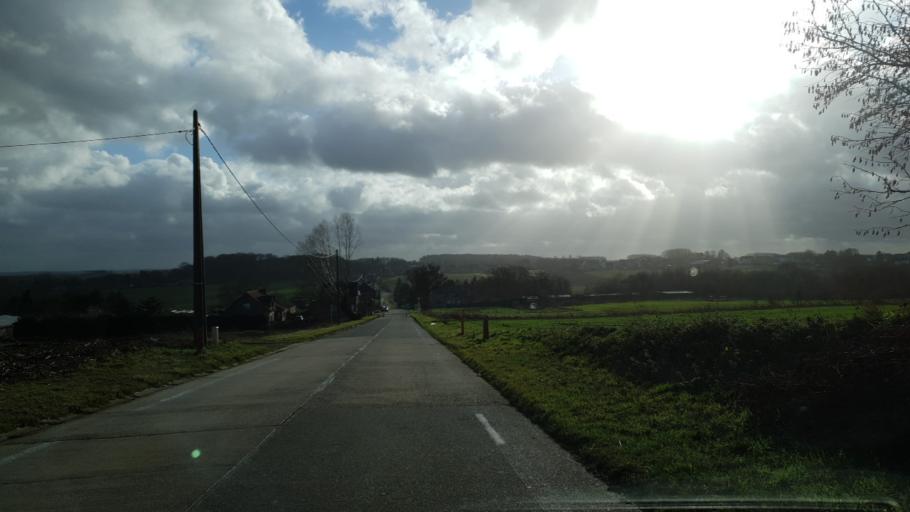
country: BE
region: Flanders
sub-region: Provincie Vlaams-Brabant
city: Kortenberg
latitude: 50.8618
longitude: 4.5806
